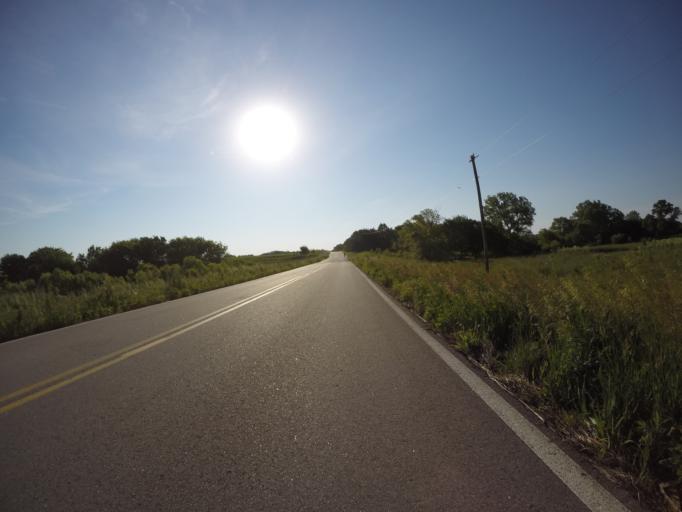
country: US
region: Nebraska
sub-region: Gage County
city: Wymore
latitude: 40.1027
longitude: -96.5221
